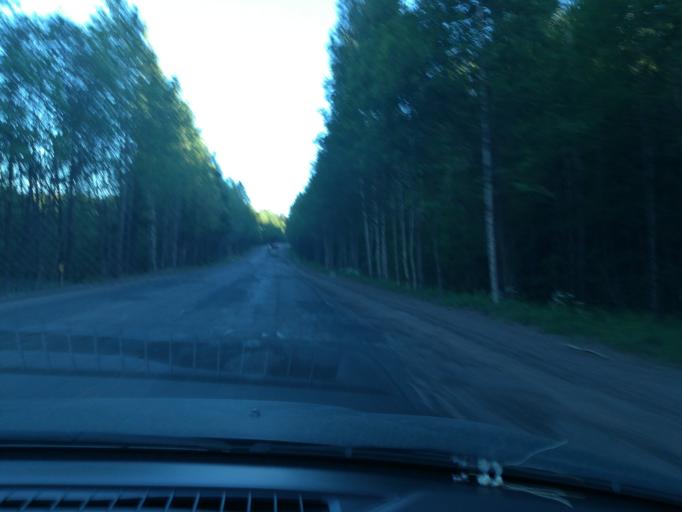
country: RU
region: Leningrad
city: Lesogorskiy
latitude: 60.9803
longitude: 28.9091
